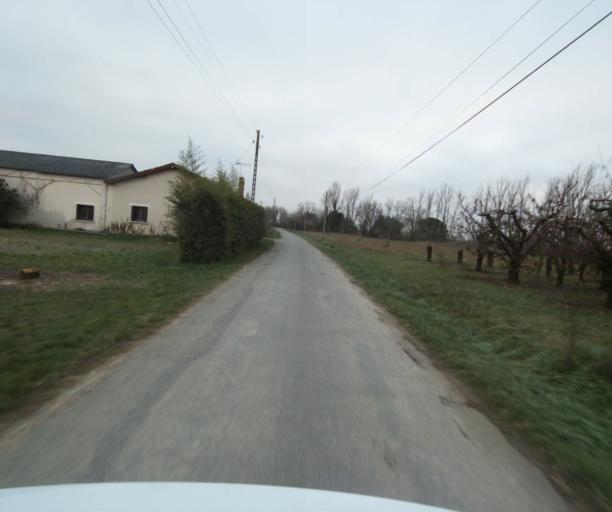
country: FR
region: Midi-Pyrenees
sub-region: Departement du Tarn-et-Garonne
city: Moissac
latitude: 44.1063
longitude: 1.1183
